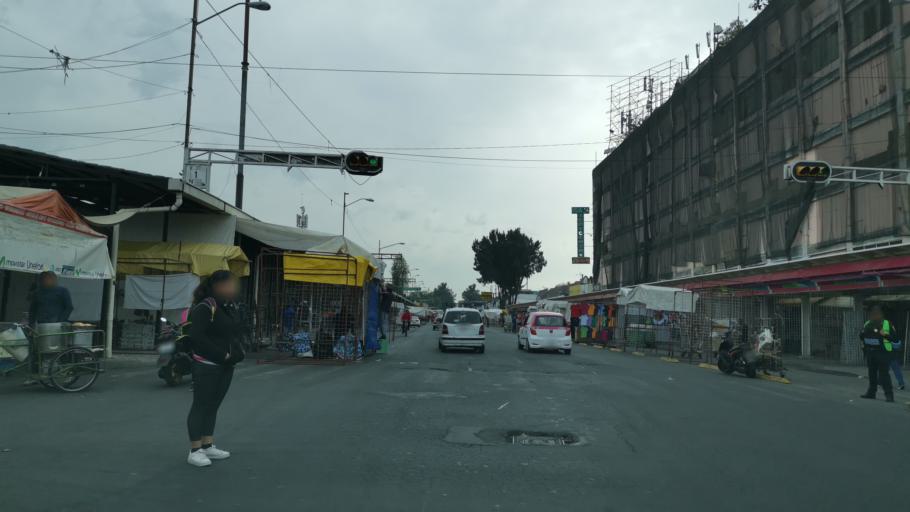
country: MX
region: Mexico City
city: Mexico City
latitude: 19.4433
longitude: -99.1308
